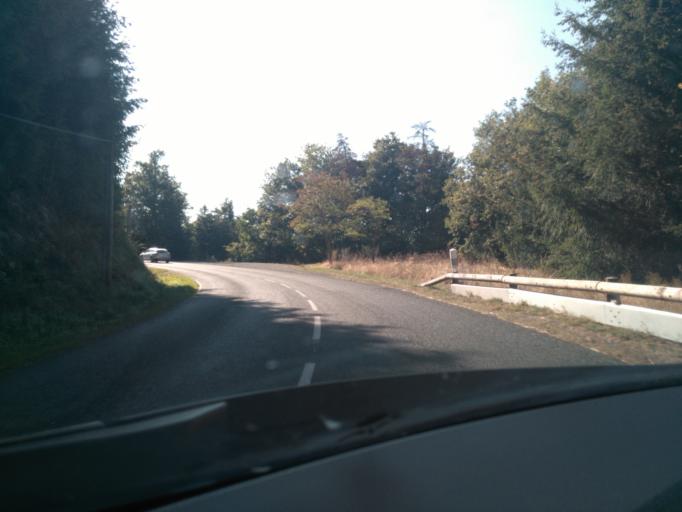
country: FR
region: Rhone-Alpes
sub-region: Departement du Rhone
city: Tarare
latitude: 45.8684
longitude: 4.4127
